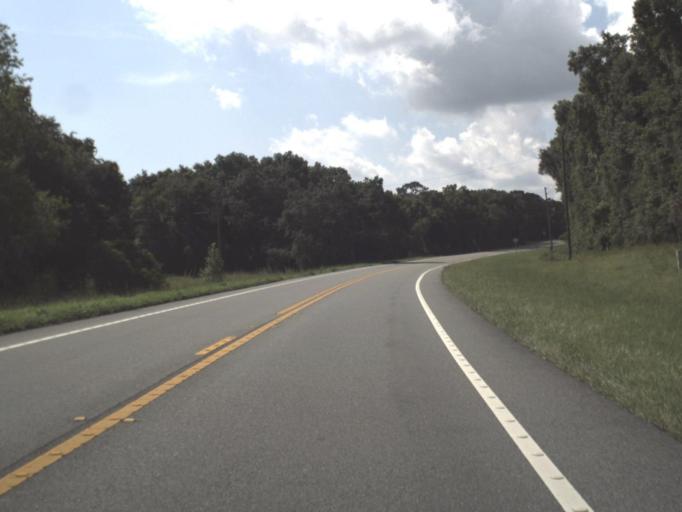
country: US
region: Florida
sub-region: Citrus County
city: Hernando
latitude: 28.9104
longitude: -82.3801
